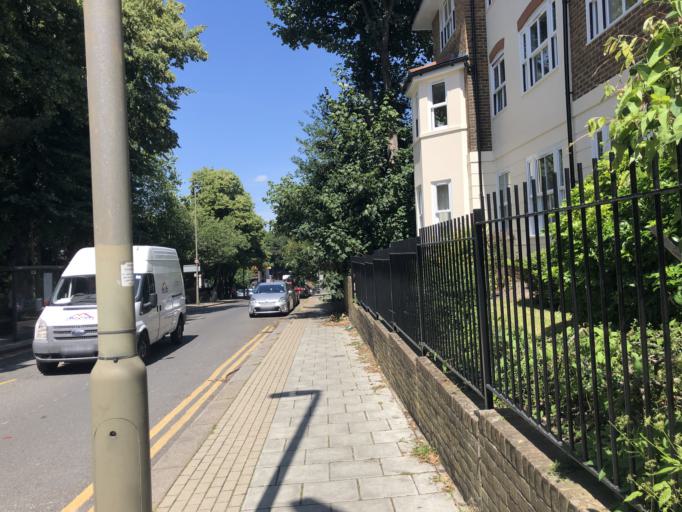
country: GB
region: England
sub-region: Greater London
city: Wandsworth
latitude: 51.4479
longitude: -0.2390
